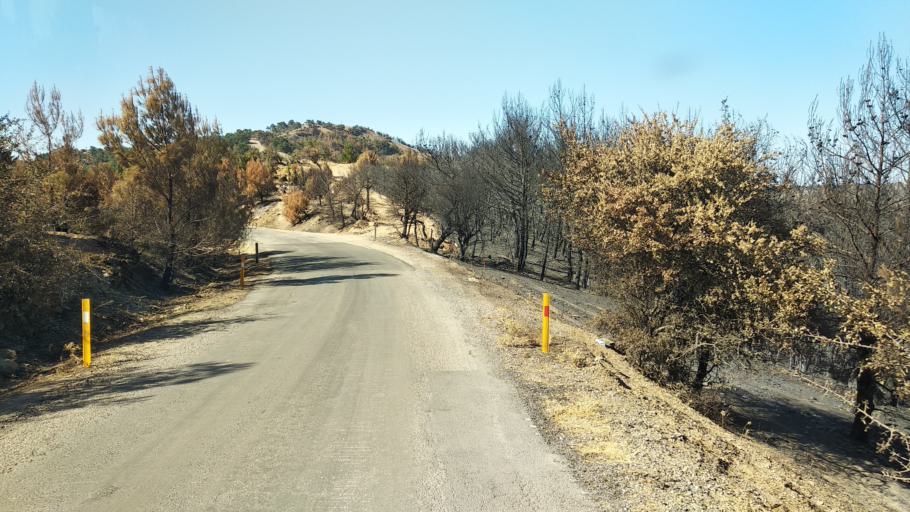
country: TR
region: Izmir
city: Gaziemir
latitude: 38.2900
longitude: 27.0020
